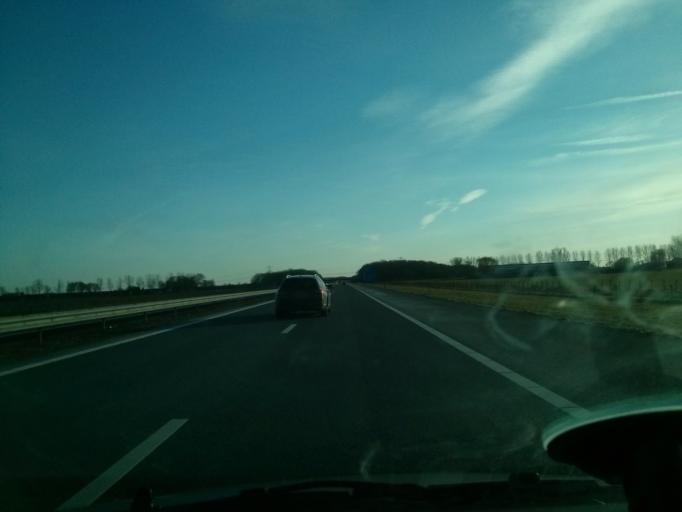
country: NL
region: Gelderland
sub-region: Gemeente Wijchen
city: Bergharen
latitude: 51.8235
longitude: 5.6820
